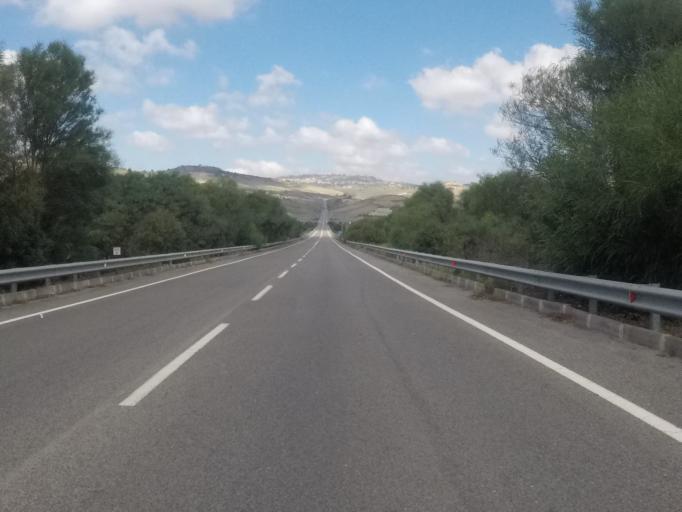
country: IT
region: Sicily
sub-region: Enna
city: Pietraperzia
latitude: 37.4490
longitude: 14.1155
